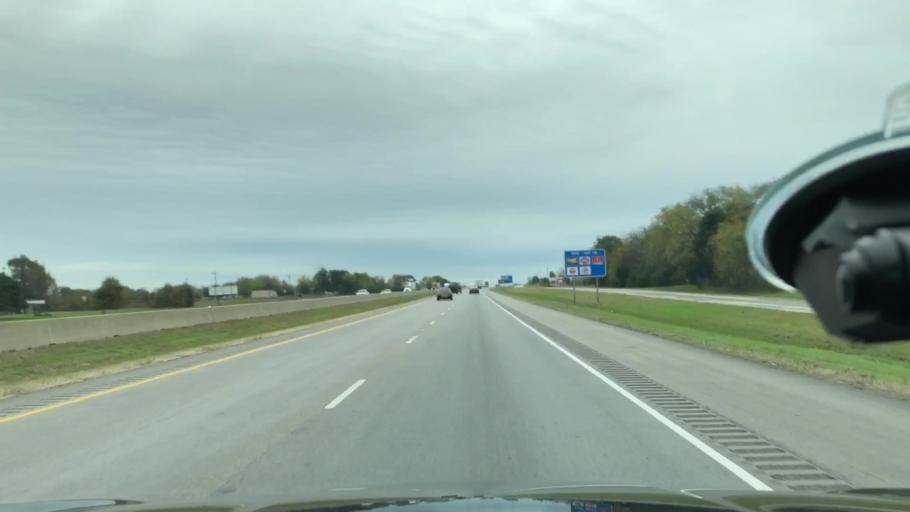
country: US
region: Texas
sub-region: Franklin County
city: Mount Vernon
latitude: 33.1631
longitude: -95.2546
